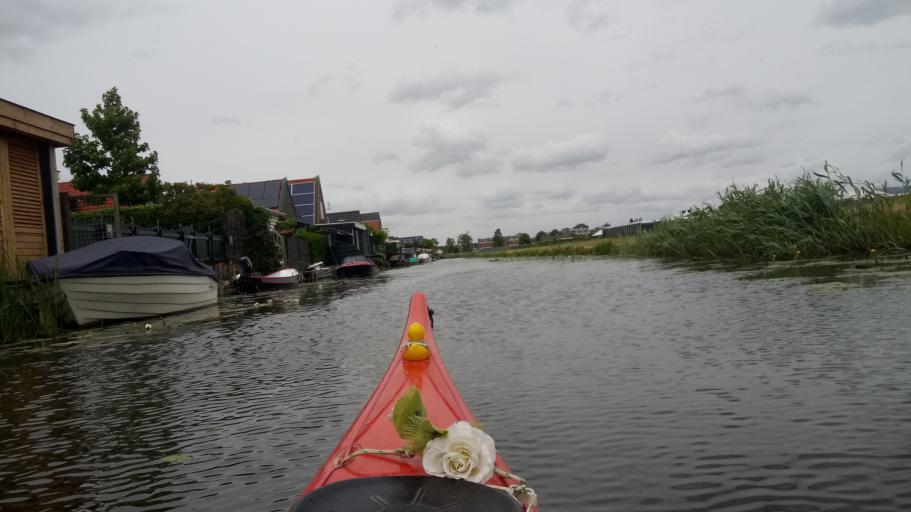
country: NL
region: North Holland
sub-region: Gemeente Enkhuizen
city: Enkhuizen
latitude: 52.6923
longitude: 5.2544
